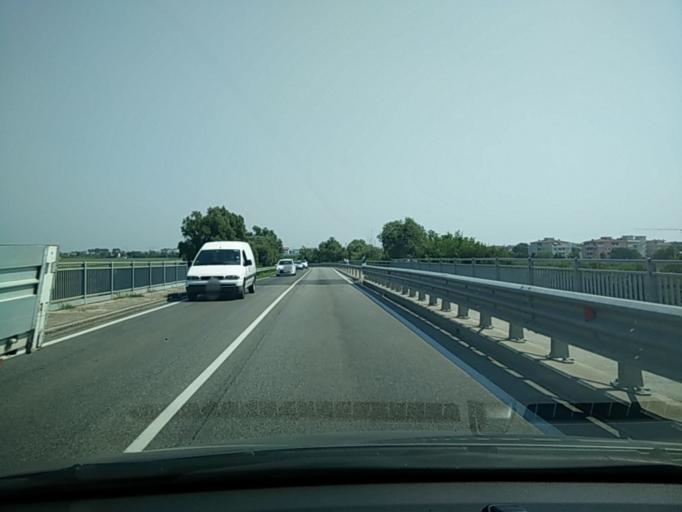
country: IT
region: Veneto
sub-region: Provincia di Venezia
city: Caorle
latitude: 45.5936
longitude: 12.8585
